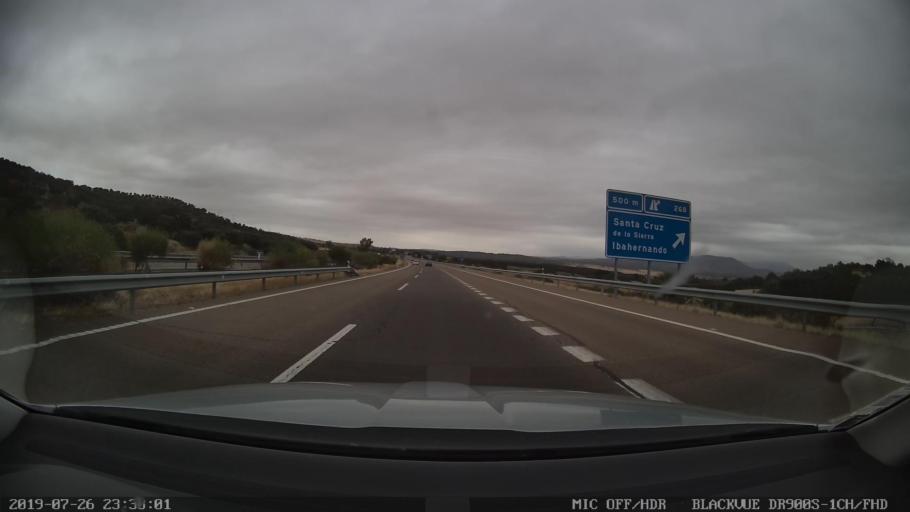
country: ES
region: Extremadura
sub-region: Provincia de Caceres
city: Santa Cruz de la Sierra
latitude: 39.3310
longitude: -5.8572
